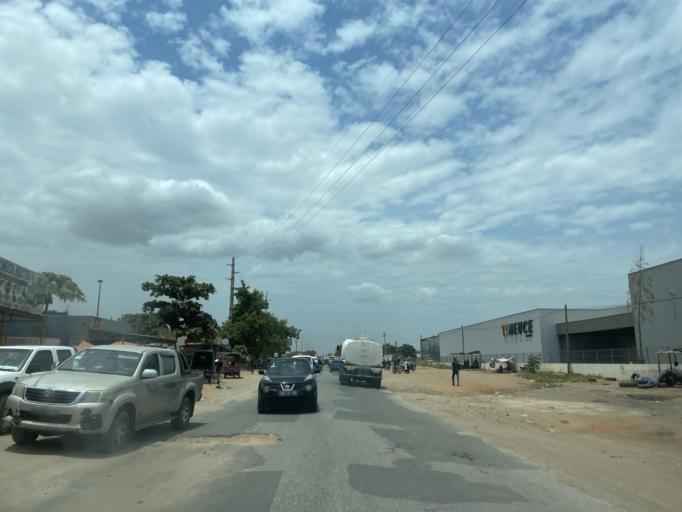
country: AO
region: Luanda
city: Luanda
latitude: -8.9469
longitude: 13.3851
